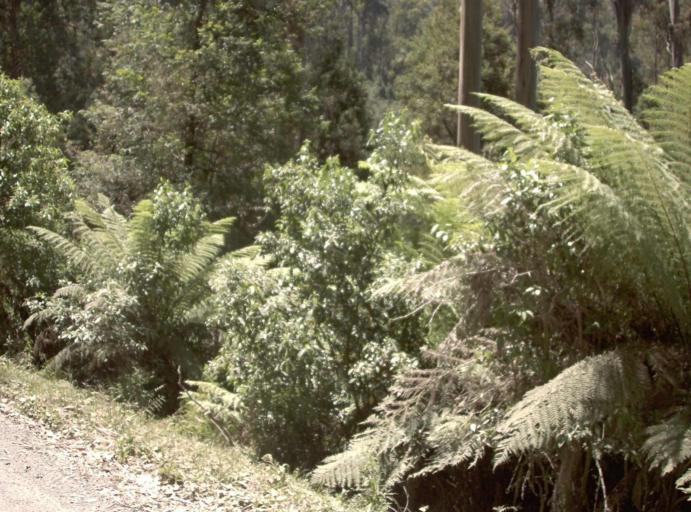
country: AU
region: Victoria
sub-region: Yarra Ranges
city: Millgrove
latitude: -37.6889
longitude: 145.7181
